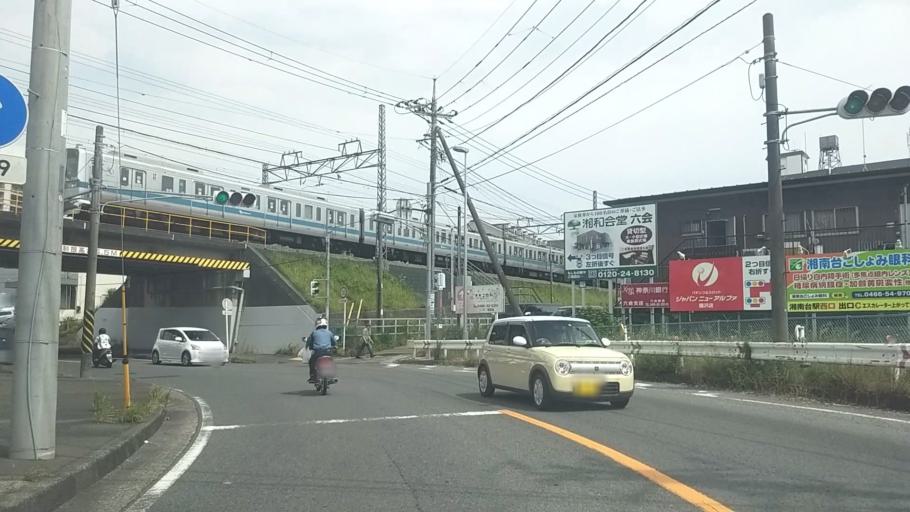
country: JP
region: Kanagawa
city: Fujisawa
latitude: 35.3865
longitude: 139.4691
